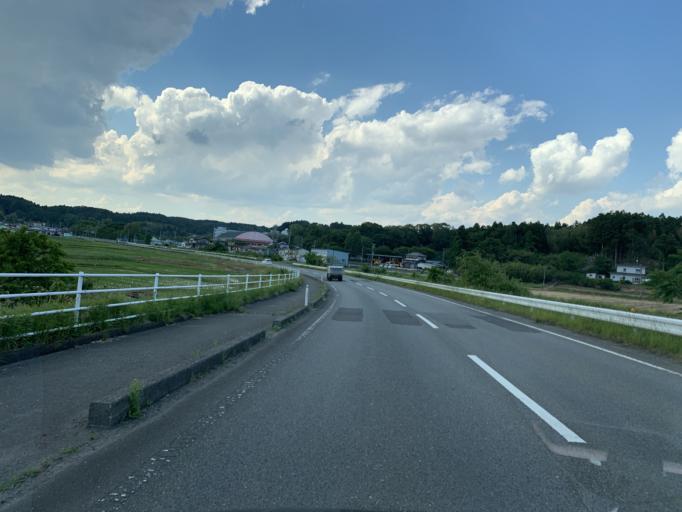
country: JP
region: Miyagi
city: Wakuya
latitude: 38.5416
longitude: 141.1493
